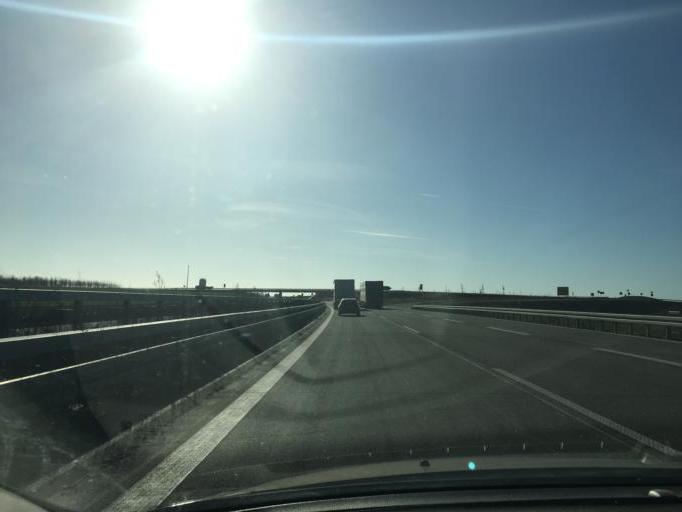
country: DE
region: Saxony
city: Geithain
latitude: 51.0510
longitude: 12.6308
